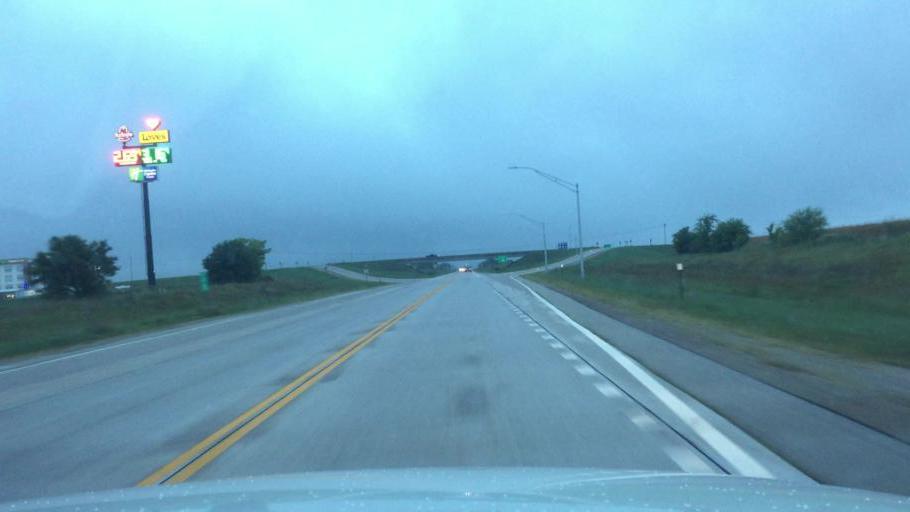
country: US
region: Kansas
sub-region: Neosho County
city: Chanute
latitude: 37.6495
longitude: -95.4797
